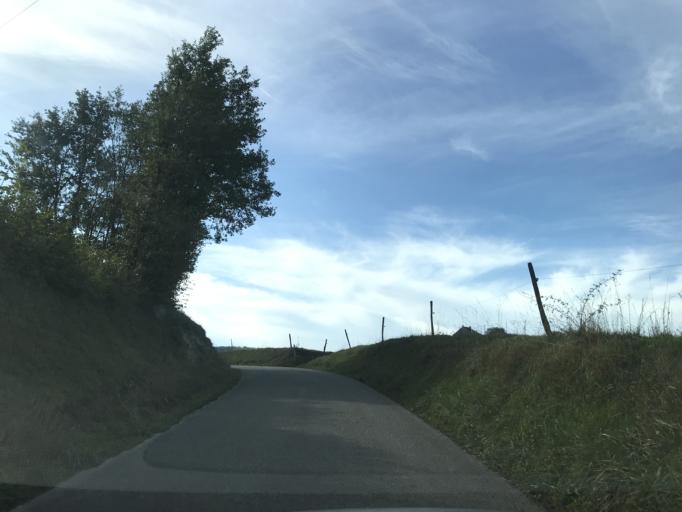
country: FR
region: Rhone-Alpes
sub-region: Departement de la Savoie
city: Yenne
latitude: 45.6879
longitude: 5.7948
